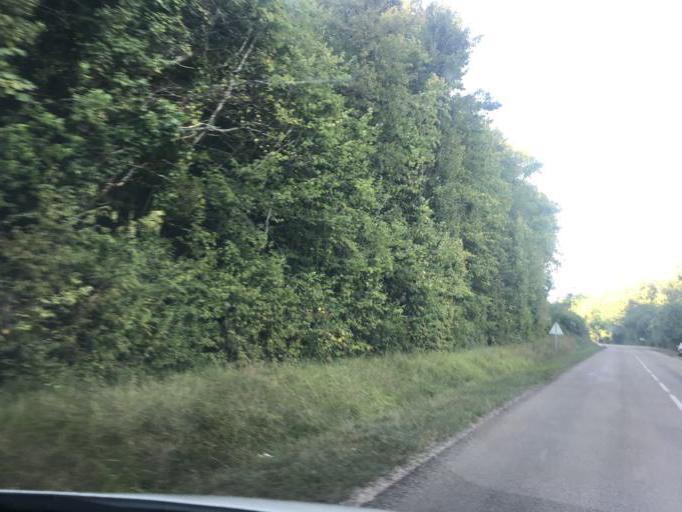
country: FR
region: Bourgogne
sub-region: Departement de l'Yonne
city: Fontenailles
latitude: 47.5474
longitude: 3.4262
